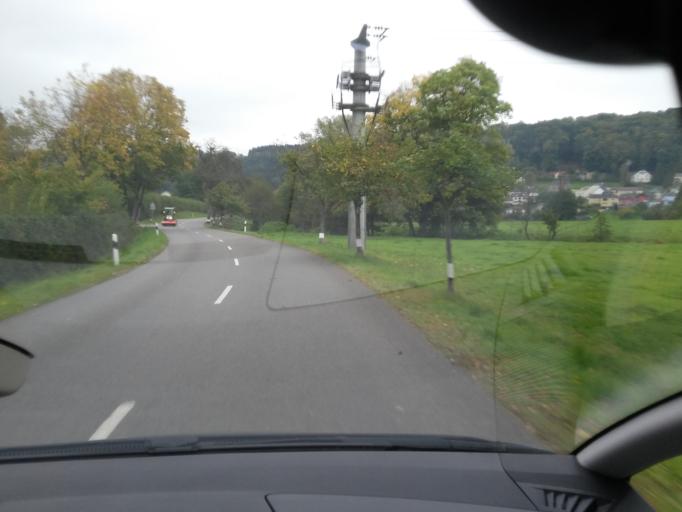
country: LU
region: Luxembourg
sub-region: Canton de Mersch
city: Tuntange
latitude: 49.6957
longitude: 5.9962
